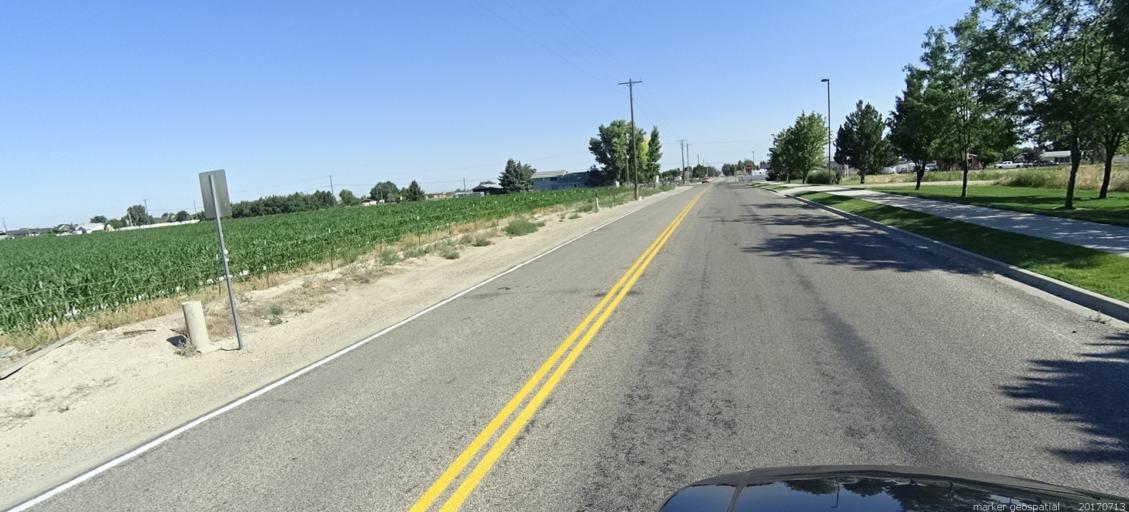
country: US
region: Idaho
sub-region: Ada County
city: Kuna
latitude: 43.5162
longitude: -116.4138
